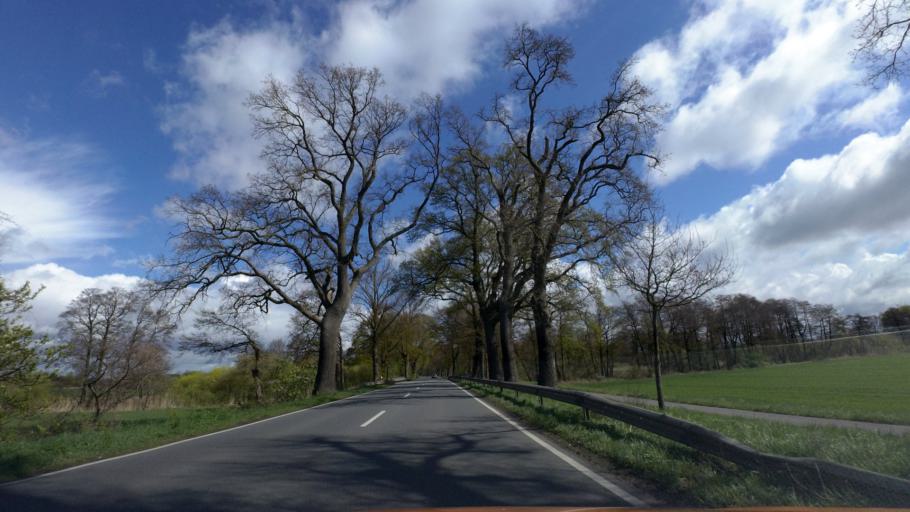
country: DE
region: Lower Saxony
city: Ottersberg
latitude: 53.1031
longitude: 9.1325
